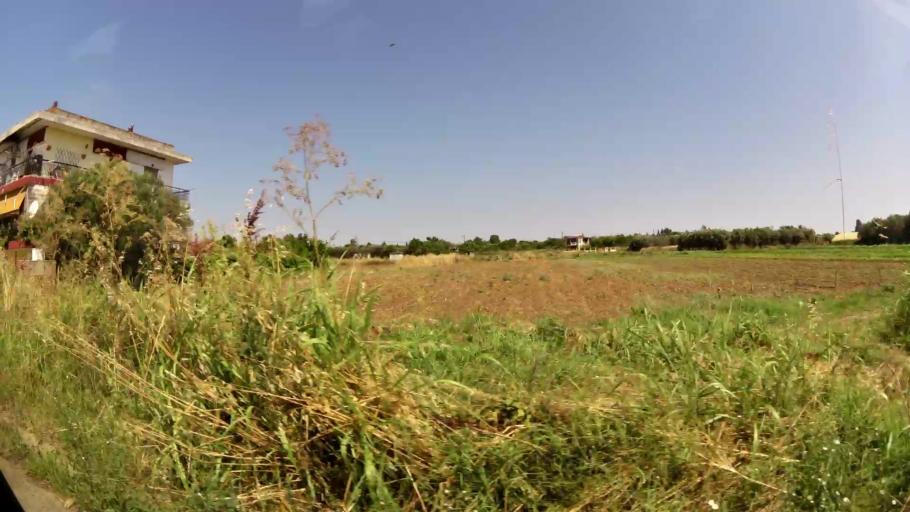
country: GR
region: Central Macedonia
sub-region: Nomos Thessalonikis
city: Nea Michaniona
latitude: 40.4947
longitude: 22.8254
